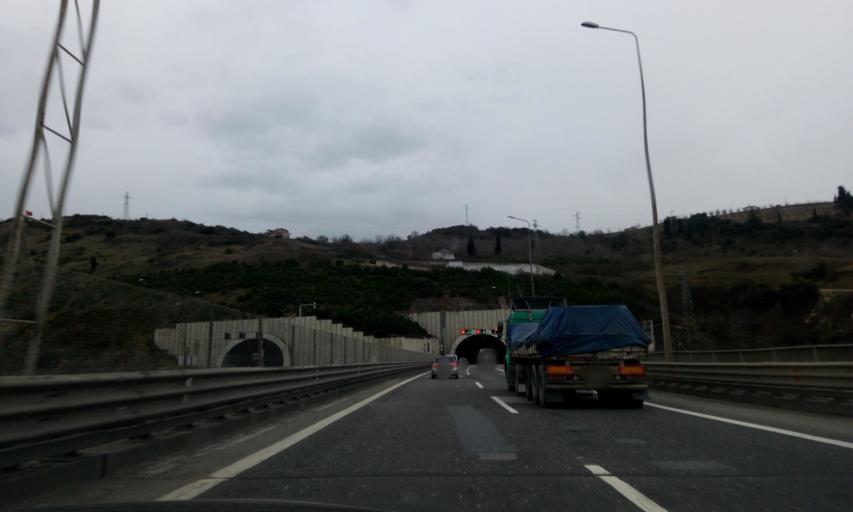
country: TR
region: Kocaeli
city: Izmit
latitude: 40.7754
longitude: 29.9019
